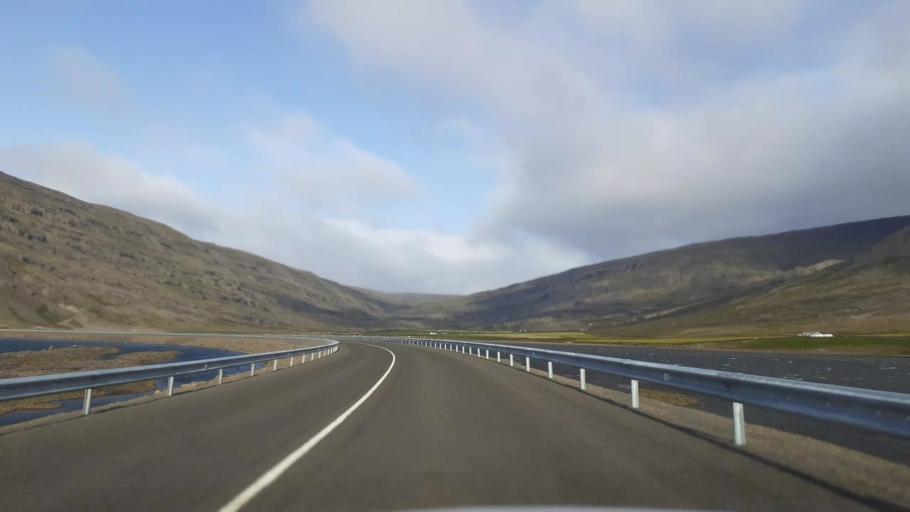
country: IS
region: East
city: Reydarfjoerdur
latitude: 64.7899
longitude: -14.4768
